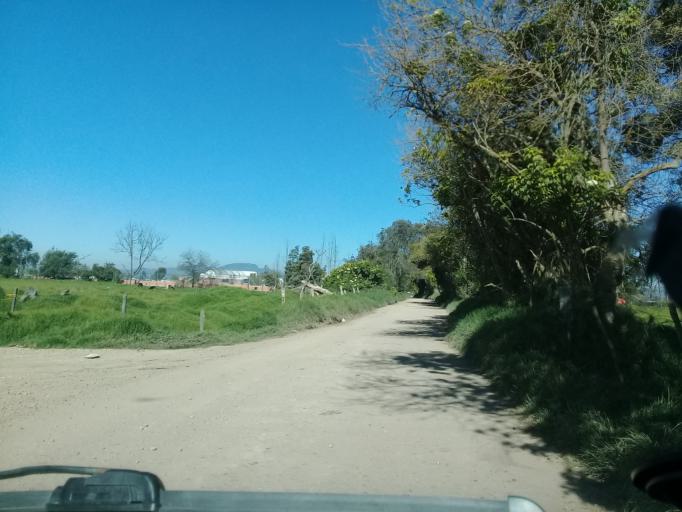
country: CO
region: Cundinamarca
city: Madrid
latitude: 4.7513
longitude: -74.2383
